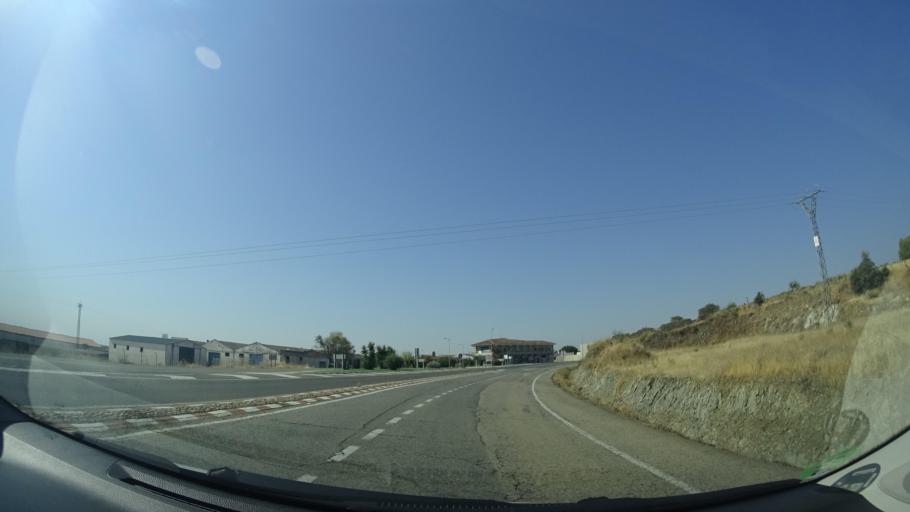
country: ES
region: Extremadura
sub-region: Provincia de Caceres
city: Miajadas
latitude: 39.1606
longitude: -5.8988
